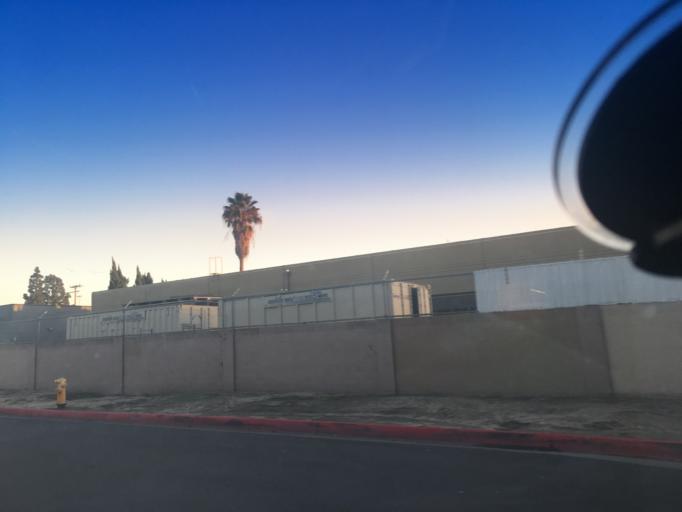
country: US
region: California
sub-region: Orange County
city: Anaheim
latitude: 33.8167
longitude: -117.8849
